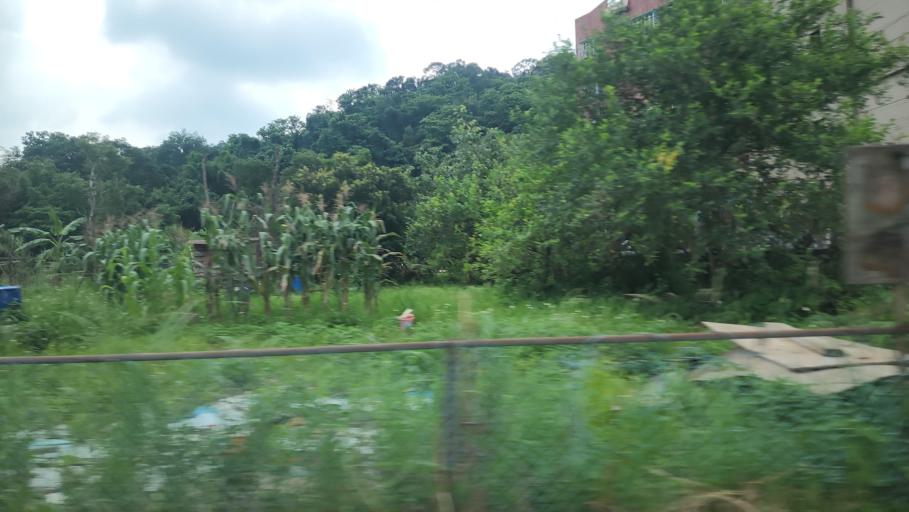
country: TW
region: Taiwan
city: Daxi
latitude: 24.9102
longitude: 121.3621
